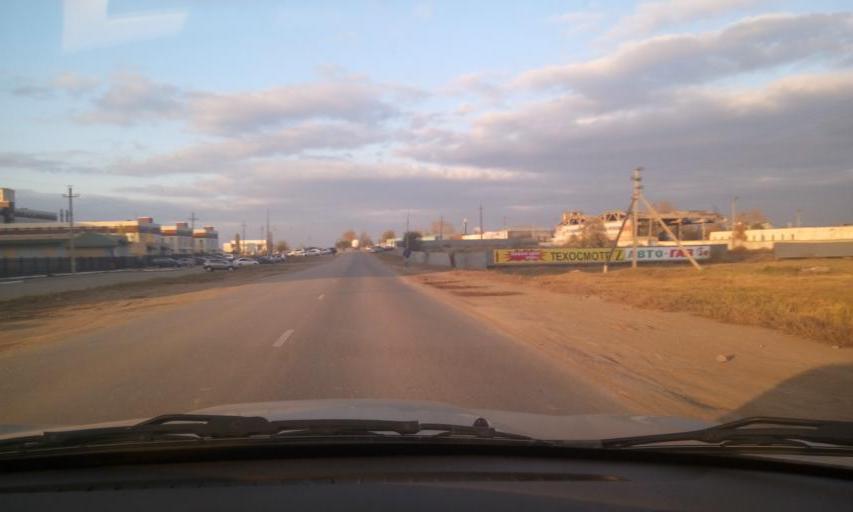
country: KZ
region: Astana Qalasy
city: Astana
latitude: 51.1395
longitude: 71.5297
